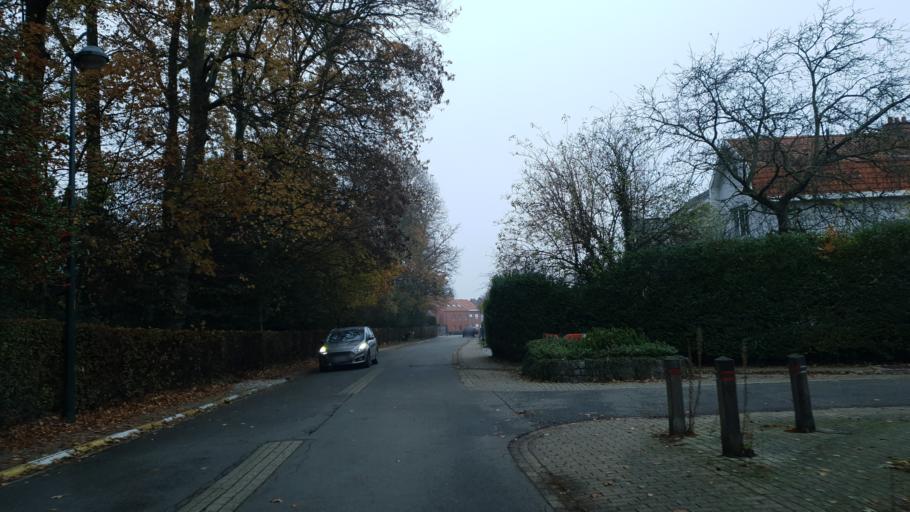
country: BE
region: Flanders
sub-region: Provincie Vlaams-Brabant
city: Kortenberg
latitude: 50.8841
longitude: 4.5363
